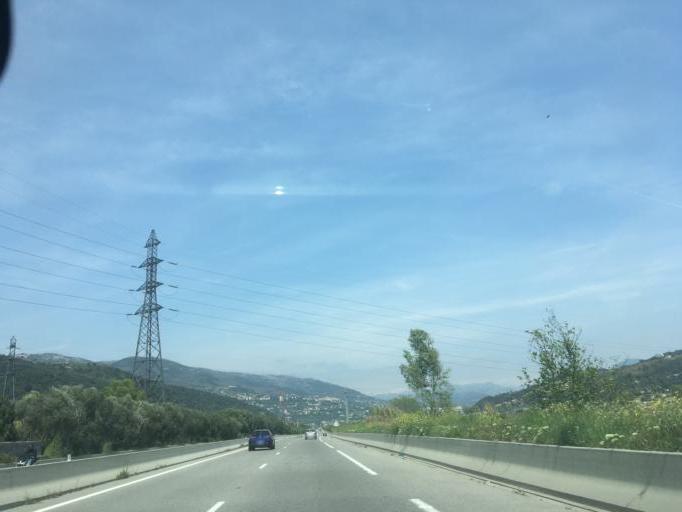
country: FR
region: Provence-Alpes-Cote d'Azur
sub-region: Departement des Alpes-Maritimes
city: La Gaude
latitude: 43.7142
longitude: 7.1831
